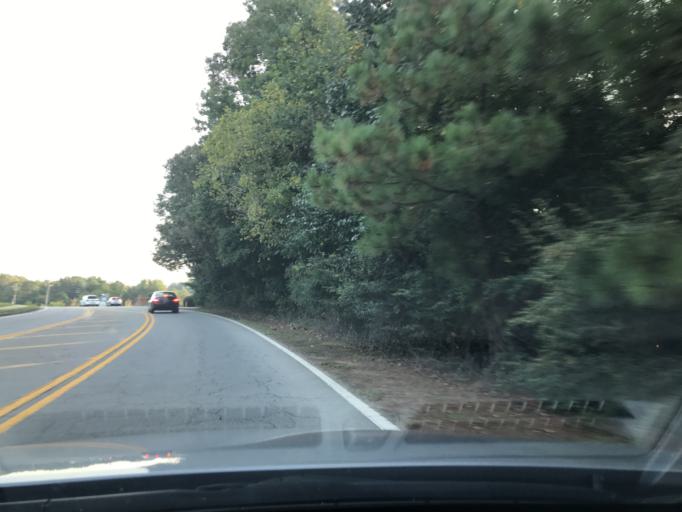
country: US
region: Georgia
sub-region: Fulton County
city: Alpharetta
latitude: 34.0714
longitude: -84.2673
